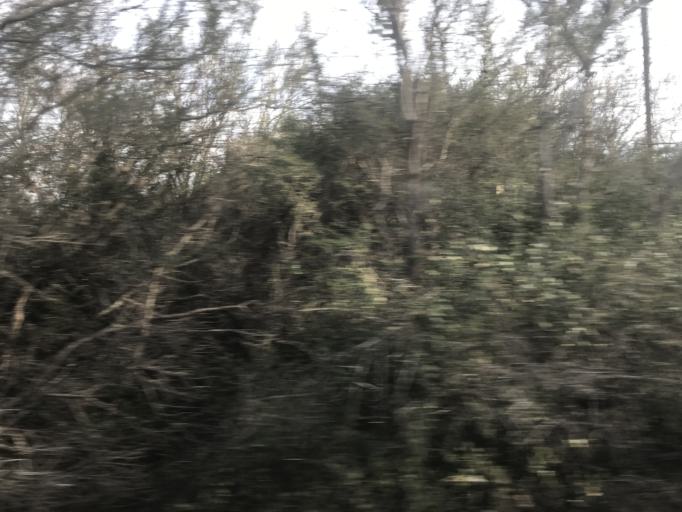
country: AR
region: Cordoba
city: Pilar
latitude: -31.7043
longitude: -63.8664
